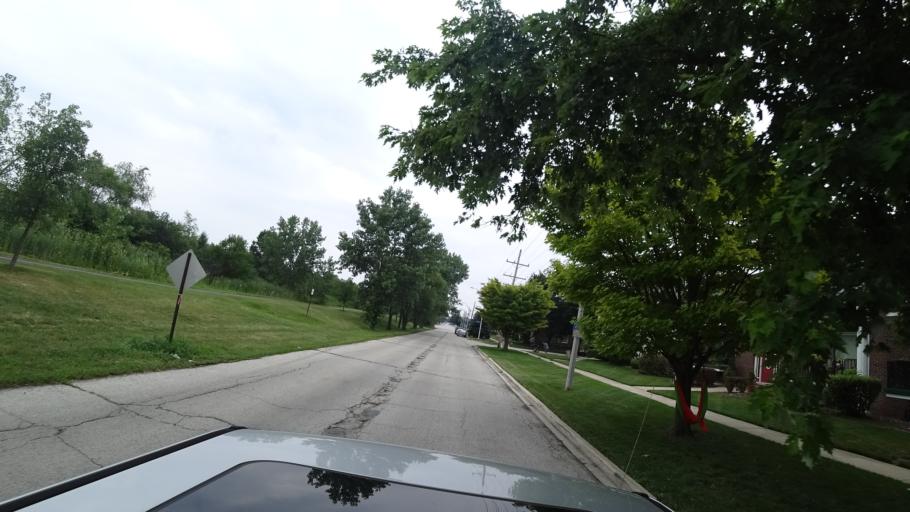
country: US
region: Illinois
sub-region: Cook County
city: Chicago Ridge
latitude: 41.7050
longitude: -87.7715
